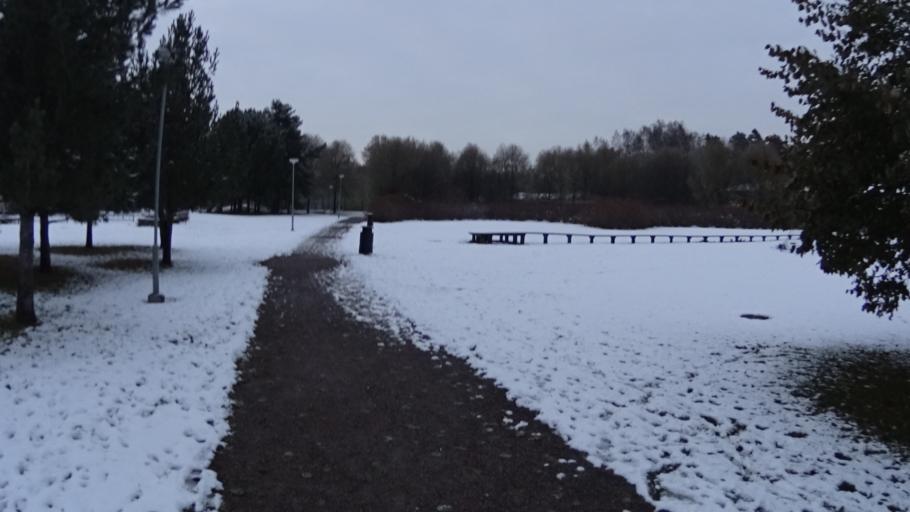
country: FI
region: Uusimaa
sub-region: Helsinki
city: Otaniemi
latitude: 60.1817
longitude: 24.8081
